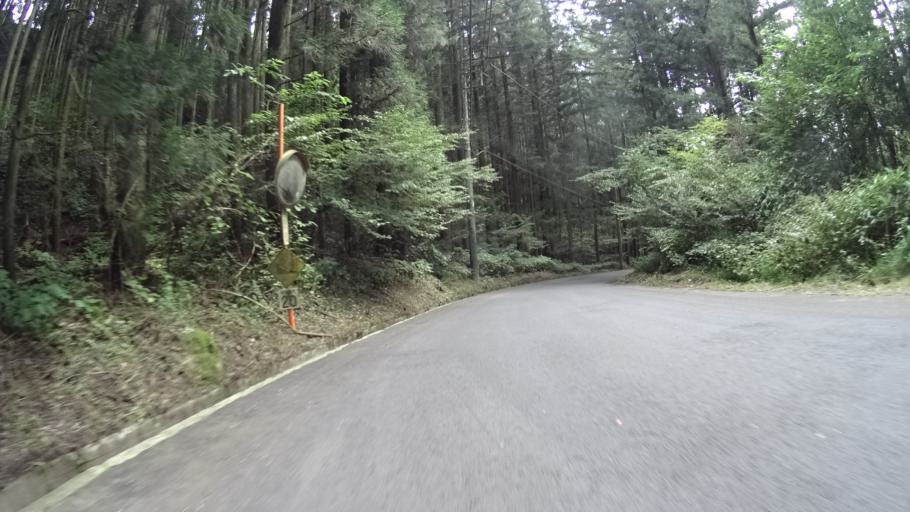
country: JP
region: Yamanashi
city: Nirasaki
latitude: 35.7848
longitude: 138.5349
